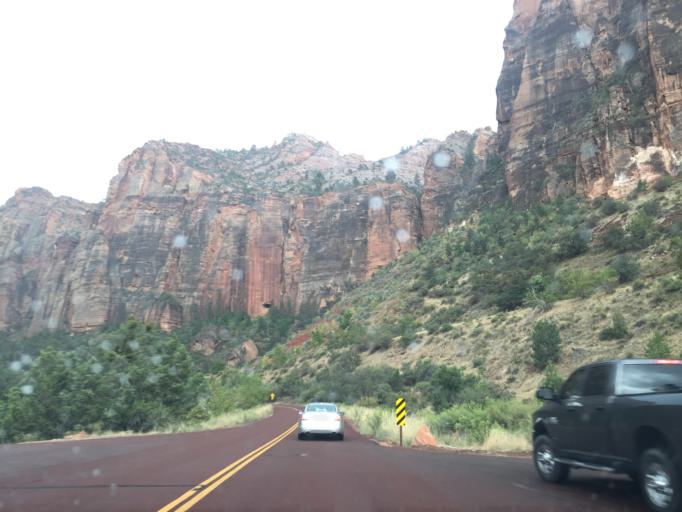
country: US
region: Utah
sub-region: Washington County
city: Hildale
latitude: 37.2134
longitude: -112.9592
